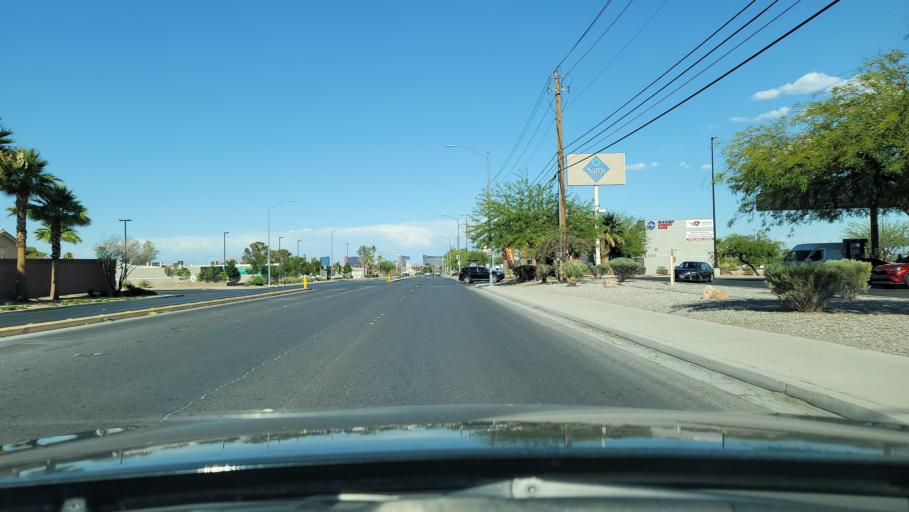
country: US
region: Nevada
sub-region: Clark County
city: Spring Valley
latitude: 36.1256
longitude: -115.2484
